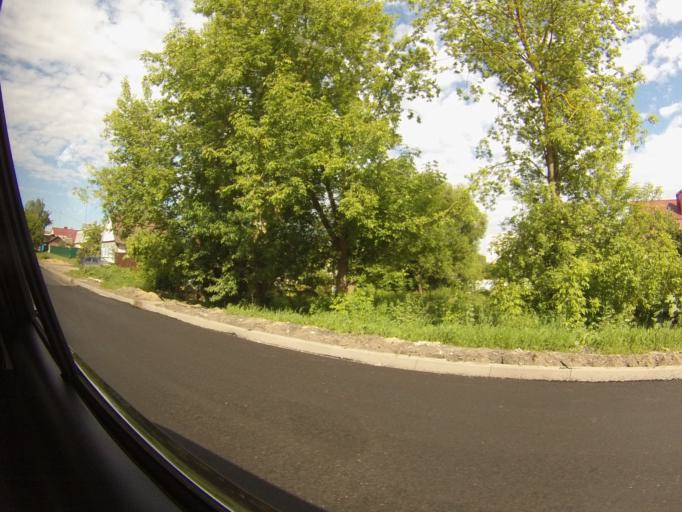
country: RU
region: Orjol
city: Mtsensk
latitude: 53.2846
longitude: 36.5782
